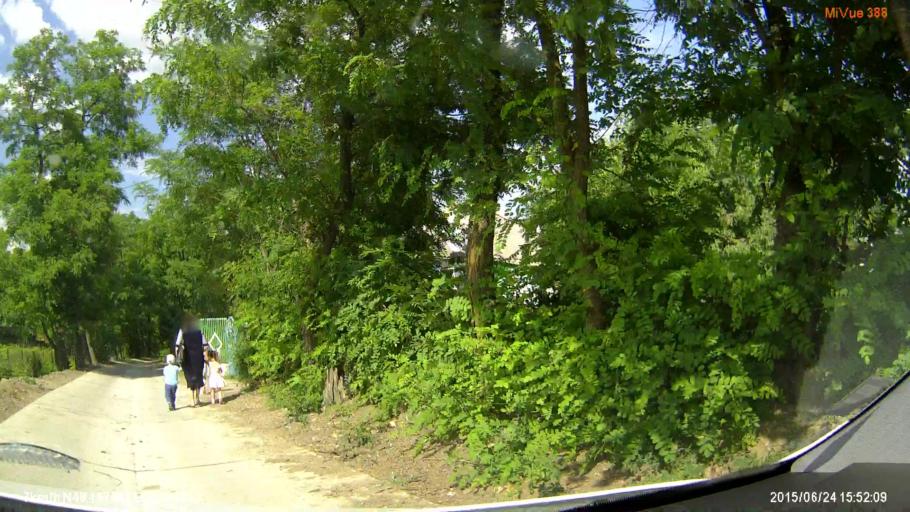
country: MD
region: Raionul Soroca
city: Soroca
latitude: 48.1674
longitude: 28.2146
